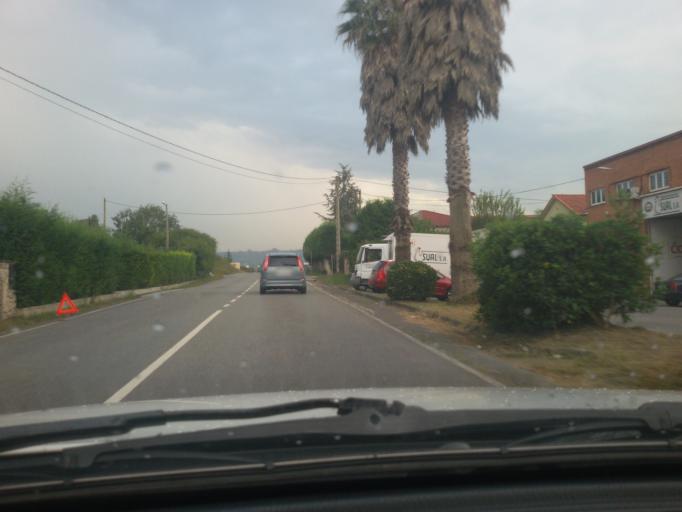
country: ES
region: Asturias
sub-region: Province of Asturias
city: Lugones
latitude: 43.3977
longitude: -5.7903
